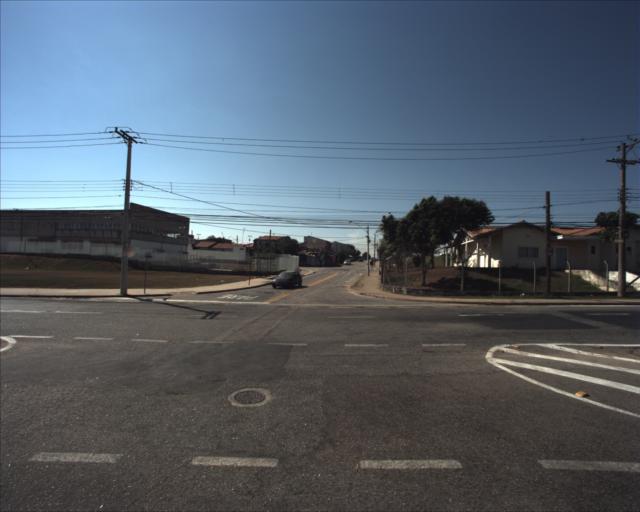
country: BR
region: Sao Paulo
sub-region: Sorocaba
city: Sorocaba
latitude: -23.4349
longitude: -47.4779
